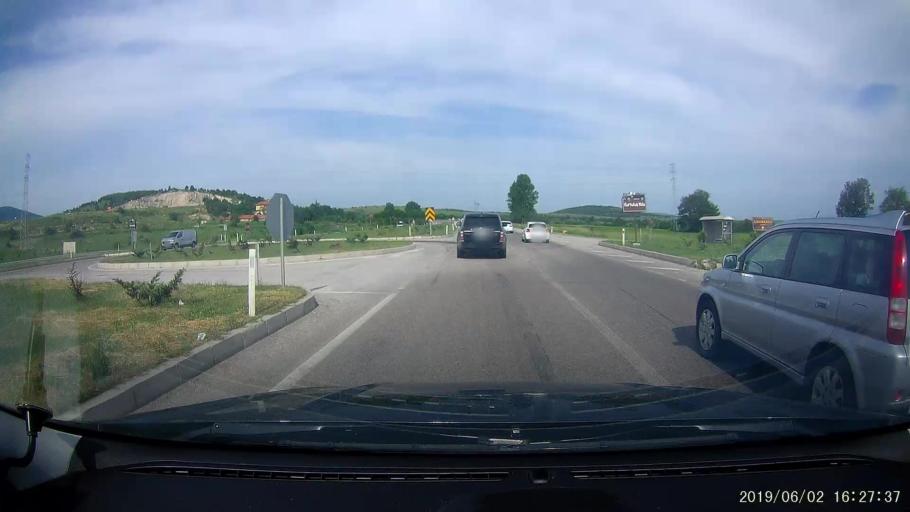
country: TR
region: Samsun
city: Ladik
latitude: 41.0022
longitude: 35.8309
